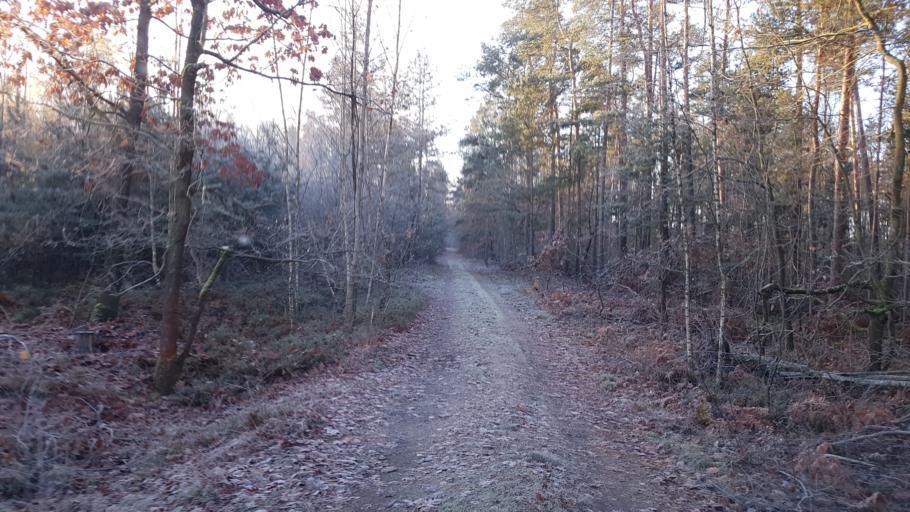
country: DE
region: Brandenburg
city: Sallgast
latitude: 51.5941
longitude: 13.8356
